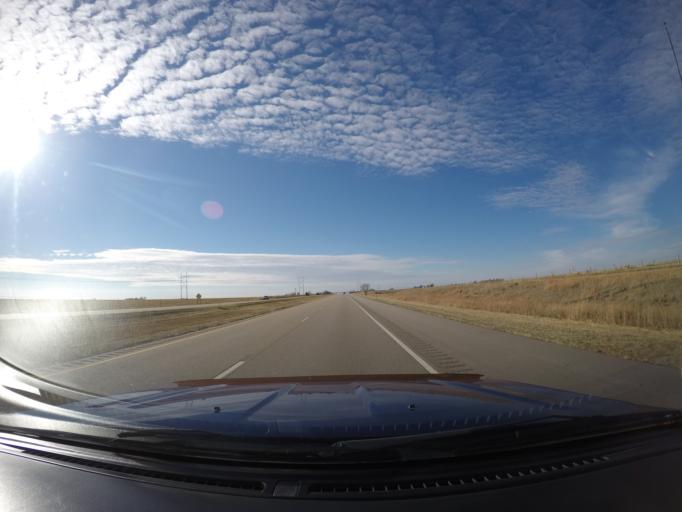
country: US
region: Nebraska
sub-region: Hamilton County
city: Aurora
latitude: 40.8221
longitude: -98.0219
